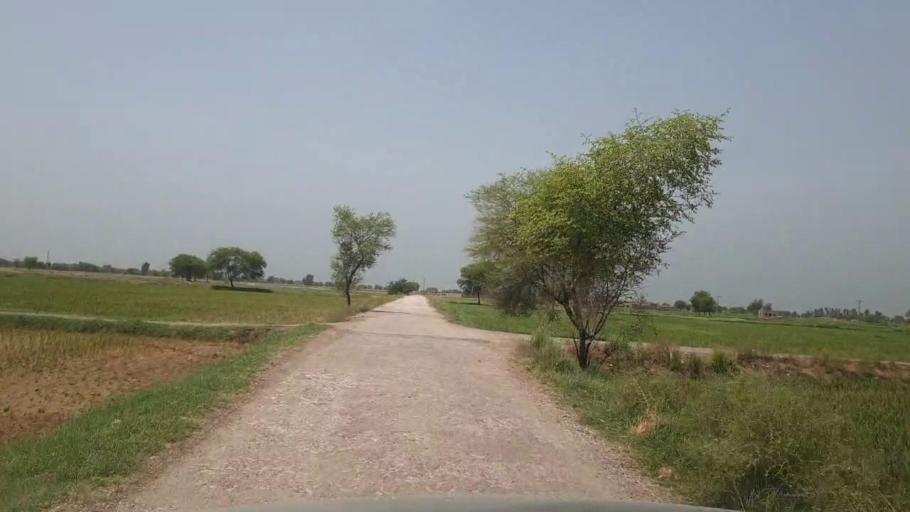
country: PK
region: Sindh
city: Ratodero
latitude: 27.9206
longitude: 68.3685
